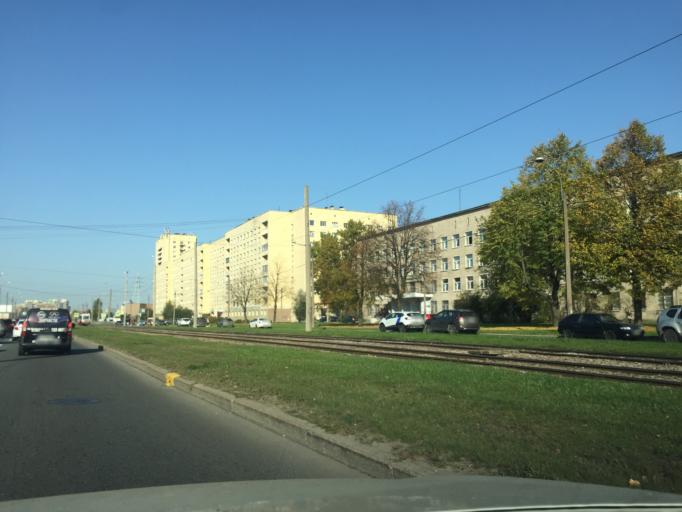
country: RU
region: St.-Petersburg
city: Grazhdanka
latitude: 60.0108
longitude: 30.4345
